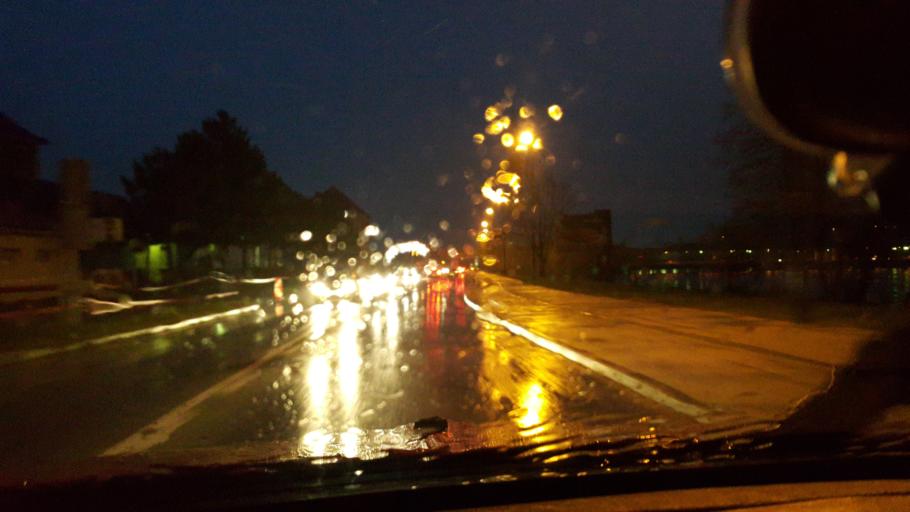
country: SI
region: Maribor
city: Maribor
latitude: 46.5565
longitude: 15.6572
